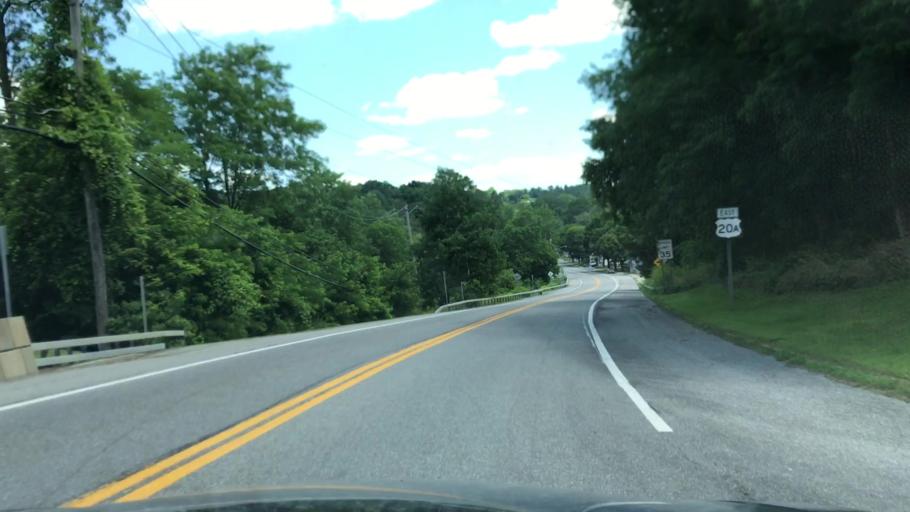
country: US
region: New York
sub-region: Erie County
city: East Aurora
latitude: 42.7685
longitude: -78.5332
